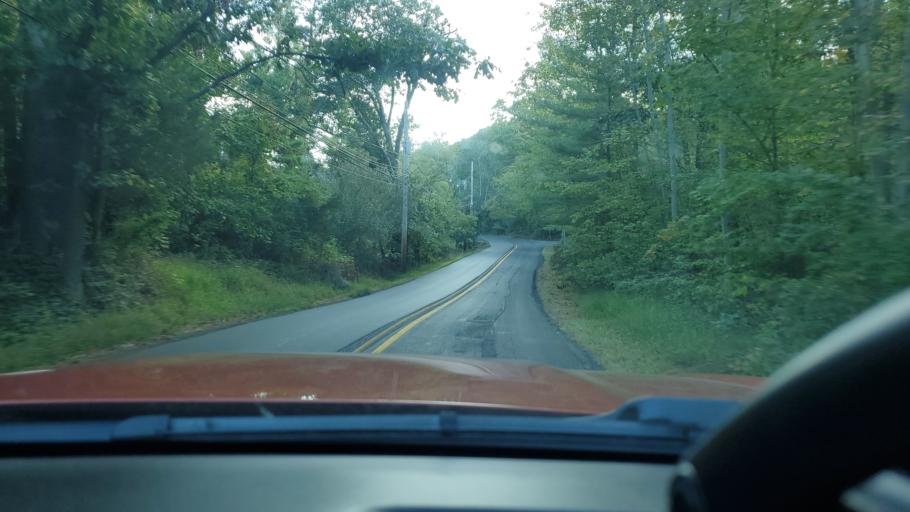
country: US
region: Pennsylvania
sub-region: Montgomery County
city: Woxall
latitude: 40.3173
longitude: -75.4915
